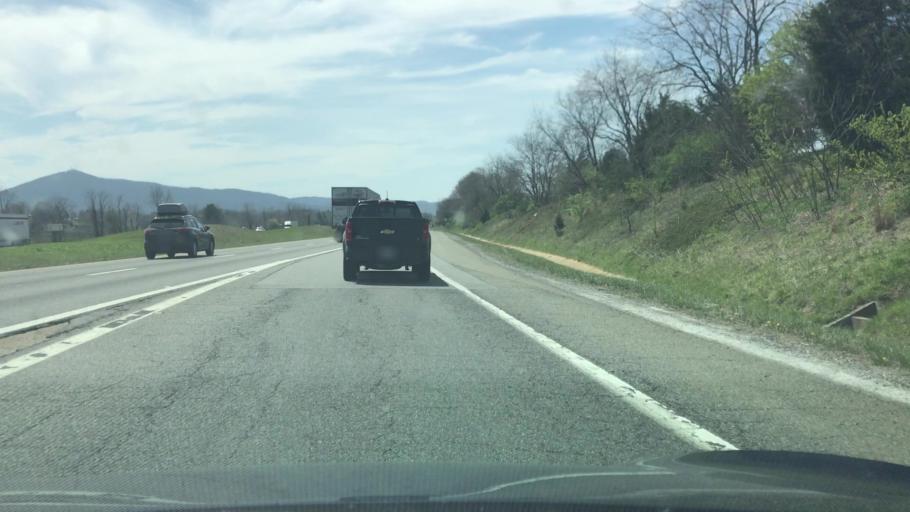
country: US
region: Virginia
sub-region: Pulaski County
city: Dublin
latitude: 37.0776
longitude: -80.6957
